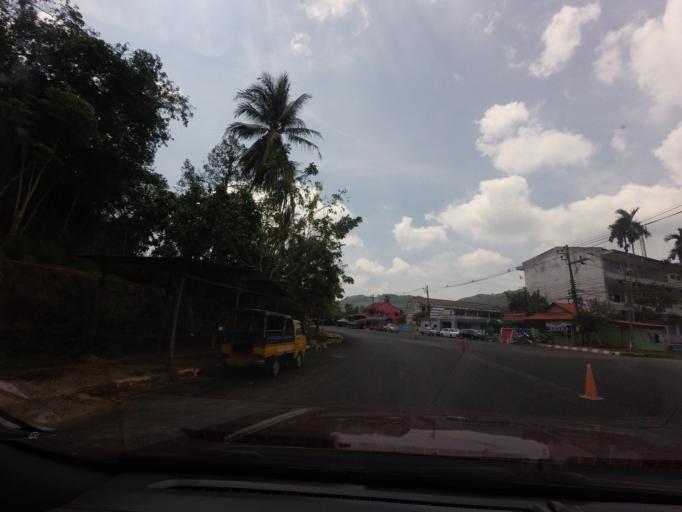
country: TH
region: Yala
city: Betong
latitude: 5.7484
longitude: 101.0359
